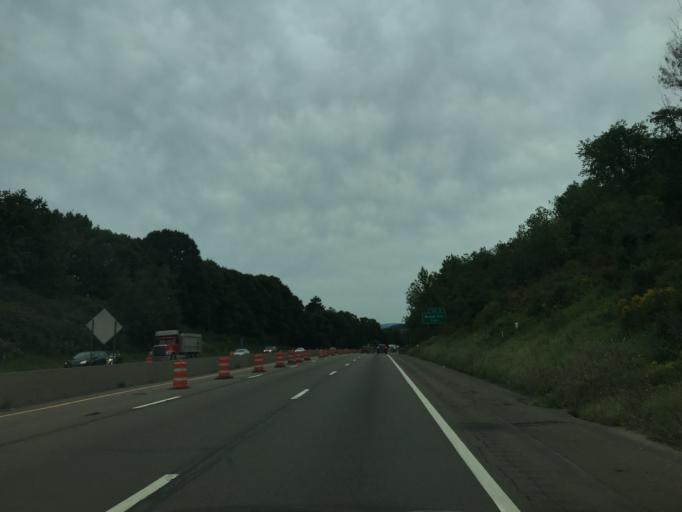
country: US
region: New York
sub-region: Broome County
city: Port Dickinson
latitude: 42.1101
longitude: -75.8657
